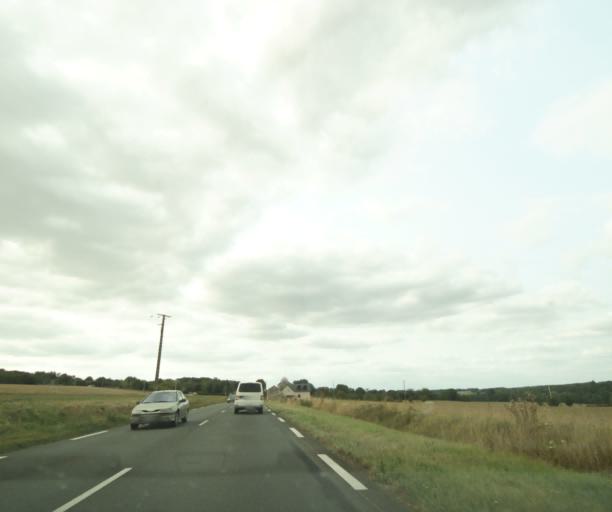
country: FR
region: Centre
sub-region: Departement d'Indre-et-Loire
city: Chambourg-sur-Indre
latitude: 47.1617
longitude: 0.9889
